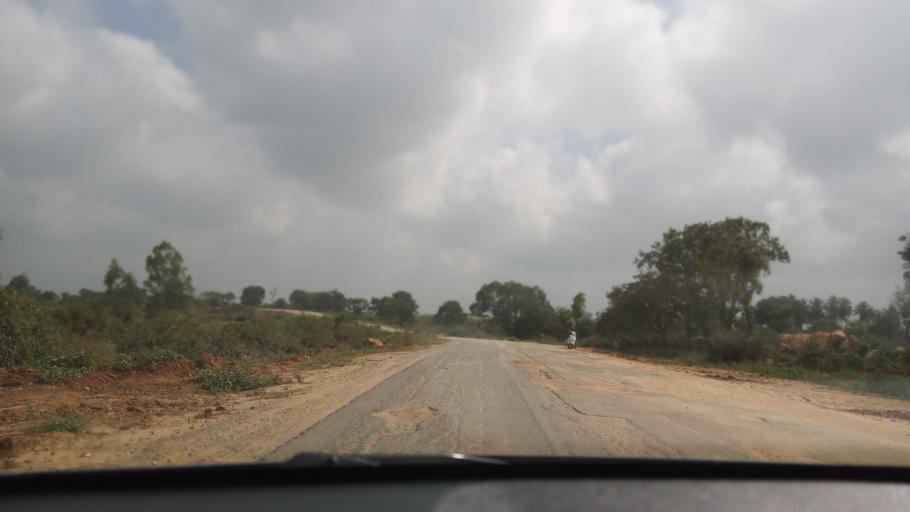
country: IN
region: Karnataka
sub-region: Kolar
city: Srinivaspur
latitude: 13.4409
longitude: 78.2299
